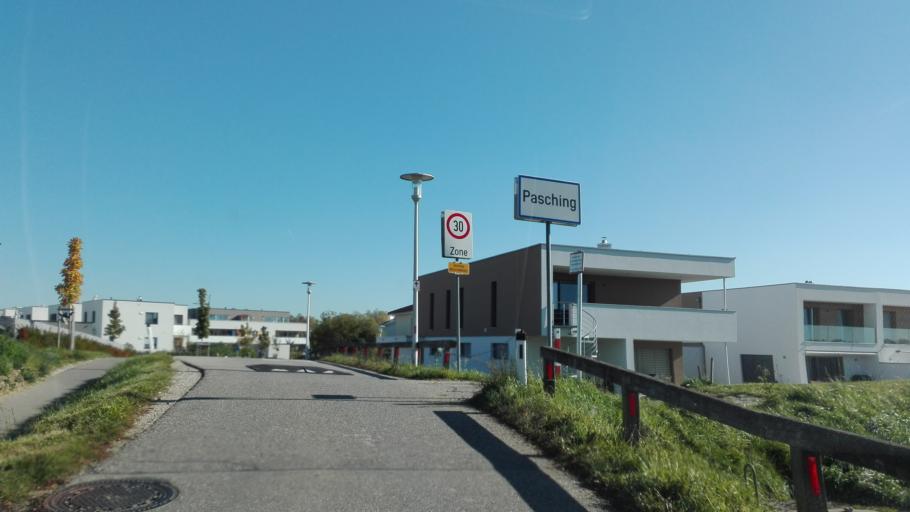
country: AT
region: Upper Austria
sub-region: Politischer Bezirk Linz-Land
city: Pasching
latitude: 48.2598
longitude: 14.1957
